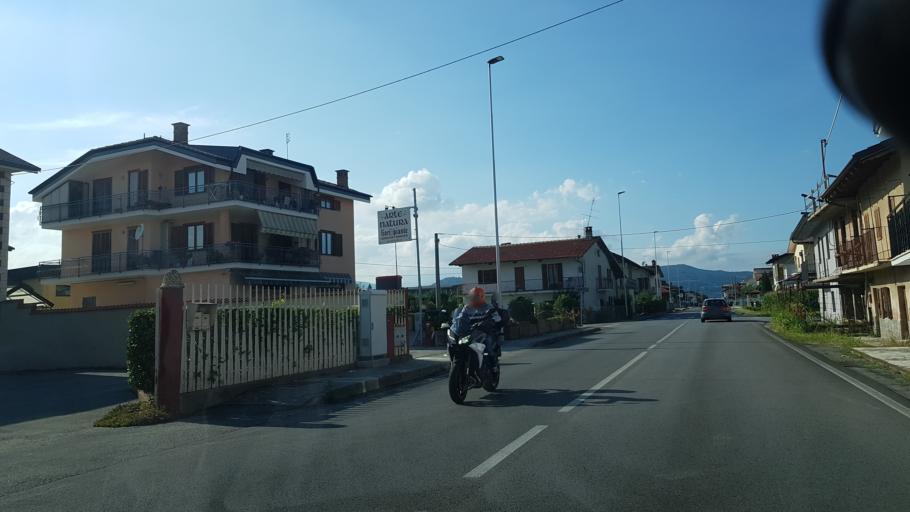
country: IT
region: Piedmont
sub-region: Provincia di Cuneo
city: Roata Rossi
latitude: 44.4779
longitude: 7.5068
